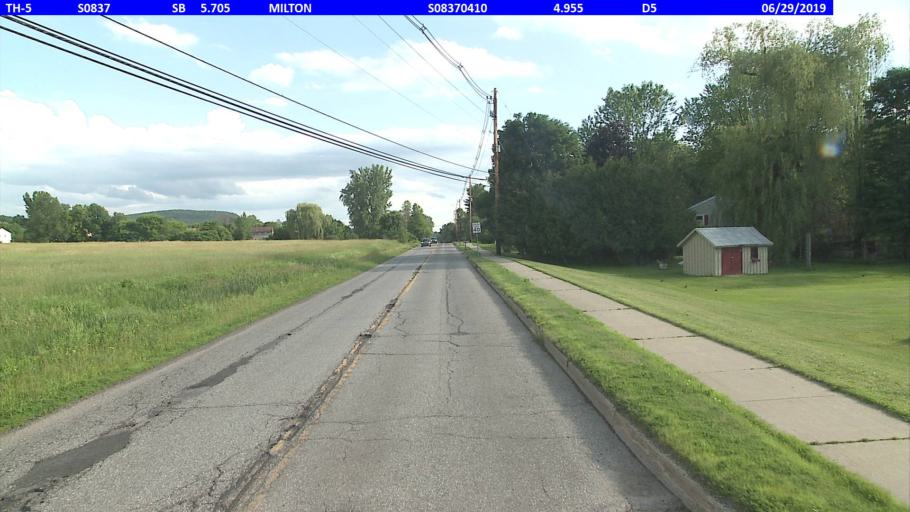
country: US
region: Vermont
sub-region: Chittenden County
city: Milton
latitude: 44.6444
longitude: -73.0996
